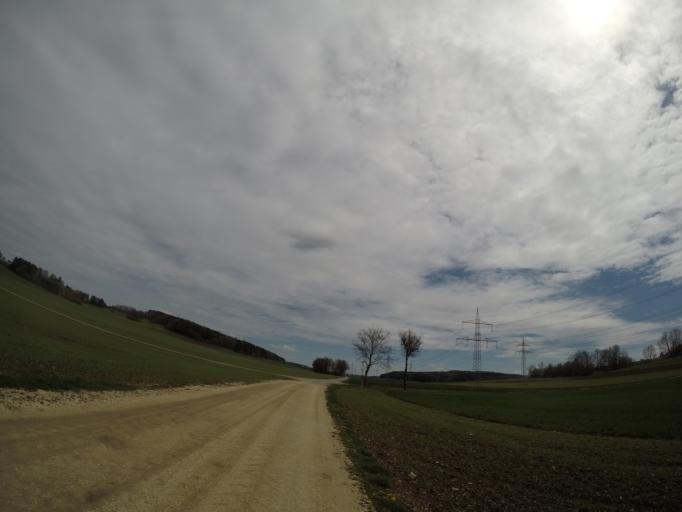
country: DE
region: Baden-Wuerttemberg
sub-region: Tuebingen Region
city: Laichingen
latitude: 48.4803
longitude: 9.6659
